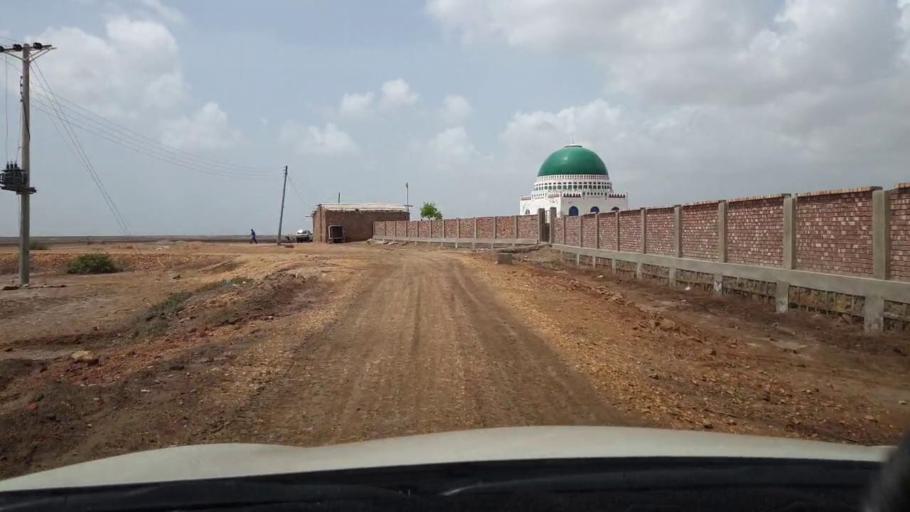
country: PK
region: Sindh
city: Kadhan
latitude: 24.3600
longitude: 68.8464
